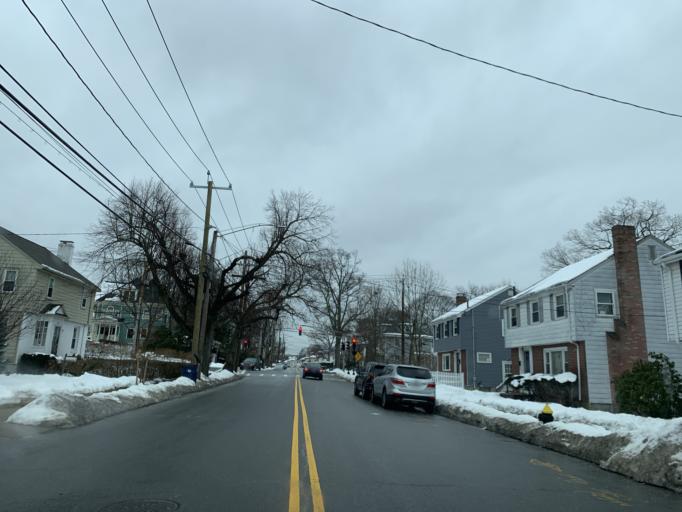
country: US
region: Massachusetts
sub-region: Norfolk County
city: Dedham
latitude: 42.2881
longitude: -71.1659
